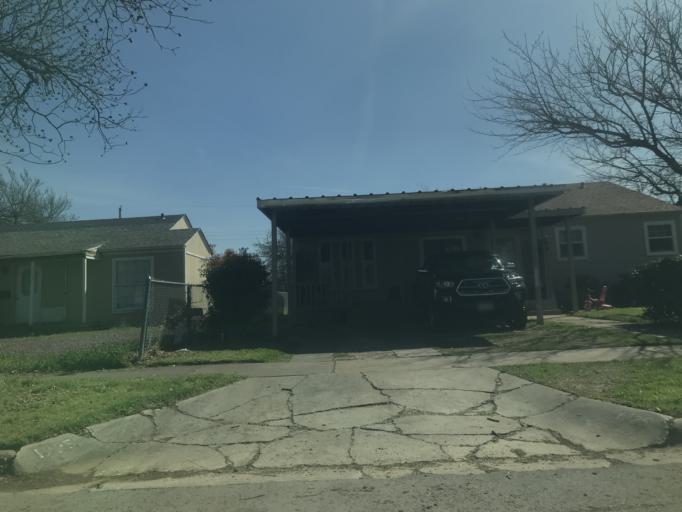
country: US
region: Texas
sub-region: Taylor County
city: Abilene
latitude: 32.4639
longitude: -99.7503
